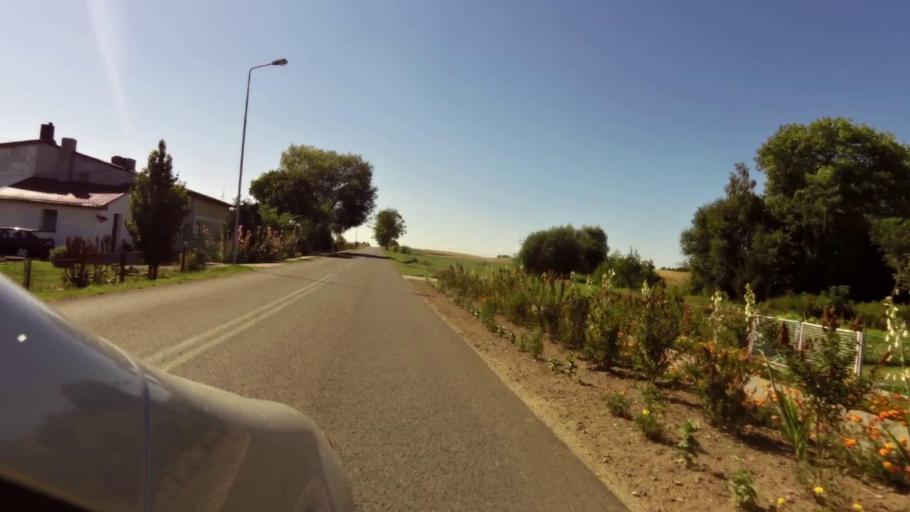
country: PL
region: West Pomeranian Voivodeship
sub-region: Powiat szczecinecki
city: Bialy Bor
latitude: 53.8180
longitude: 16.8107
